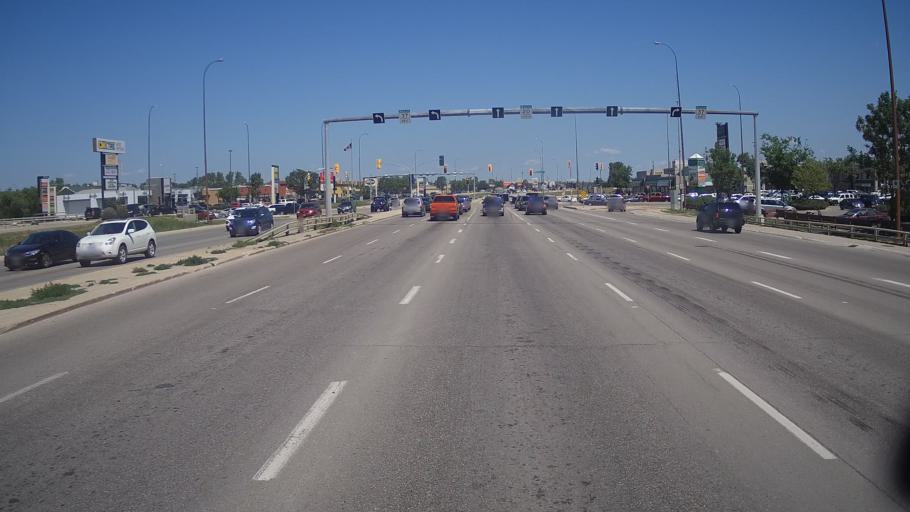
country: CA
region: Manitoba
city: Winnipeg
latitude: 49.8971
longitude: -97.0695
